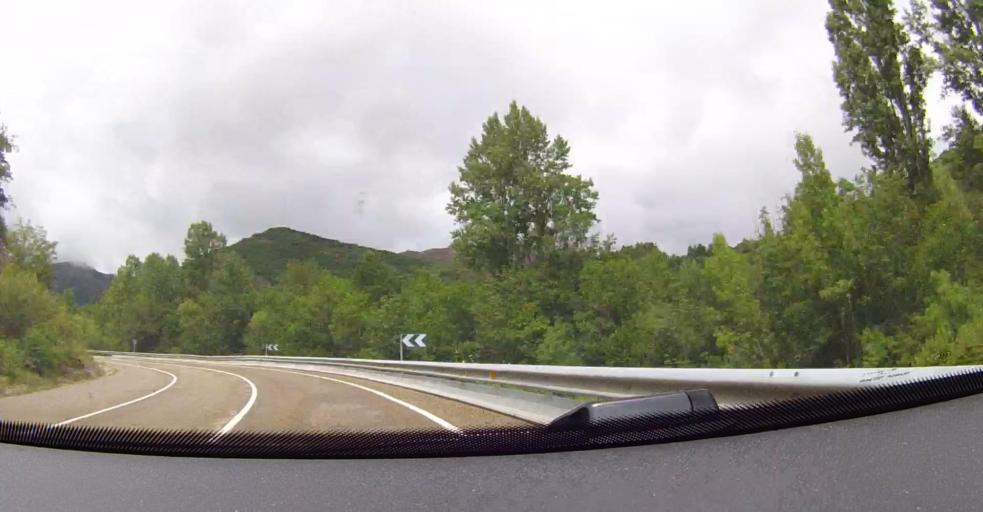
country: ES
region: Castille and Leon
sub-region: Provincia de Leon
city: Bonar
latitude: 42.8969
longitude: -5.3088
